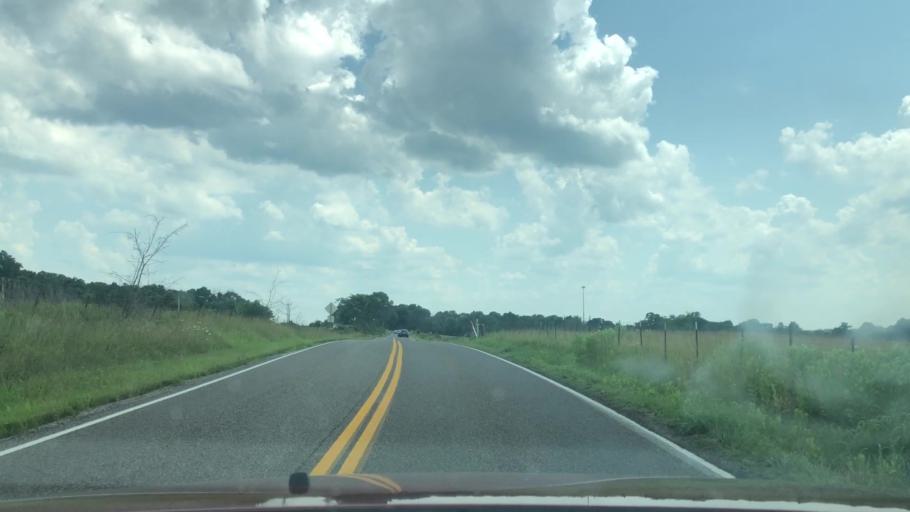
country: US
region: Missouri
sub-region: Christian County
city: Ozark
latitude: 36.9403
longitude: -93.2536
